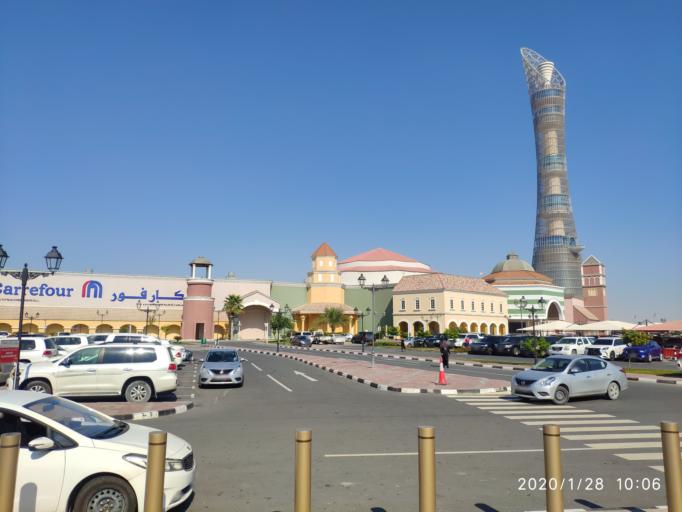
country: QA
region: Baladiyat ar Rayyan
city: Ar Rayyan
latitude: 25.2576
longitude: 51.4441
